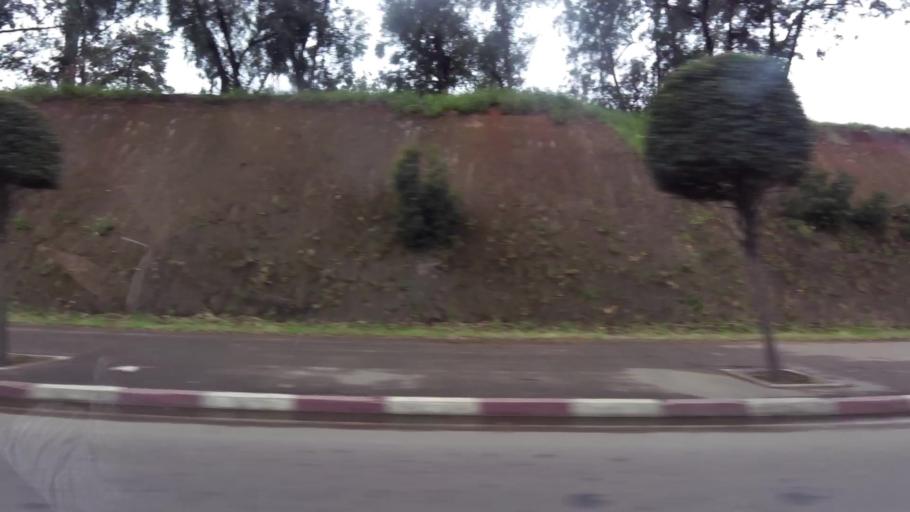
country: MA
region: Grand Casablanca
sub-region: Casablanca
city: Casablanca
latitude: 33.5314
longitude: -7.6377
